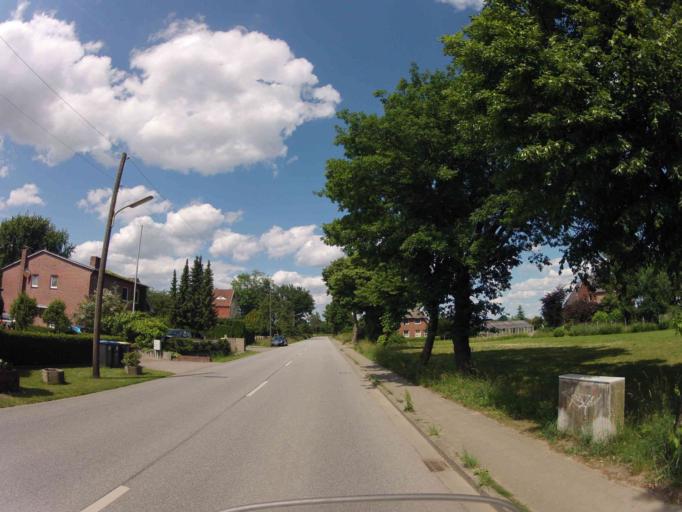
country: DE
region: Lower Saxony
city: Winsen
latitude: 53.4123
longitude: 10.1917
